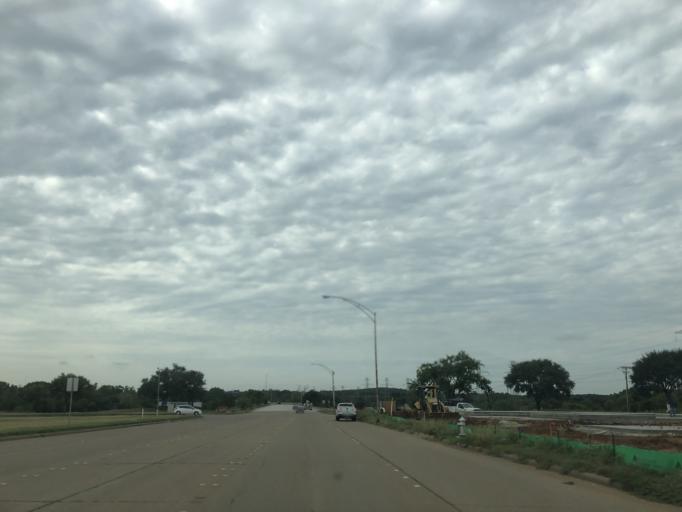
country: US
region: Texas
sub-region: Tarrant County
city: Richland Hills
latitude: 32.7859
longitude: -97.2213
